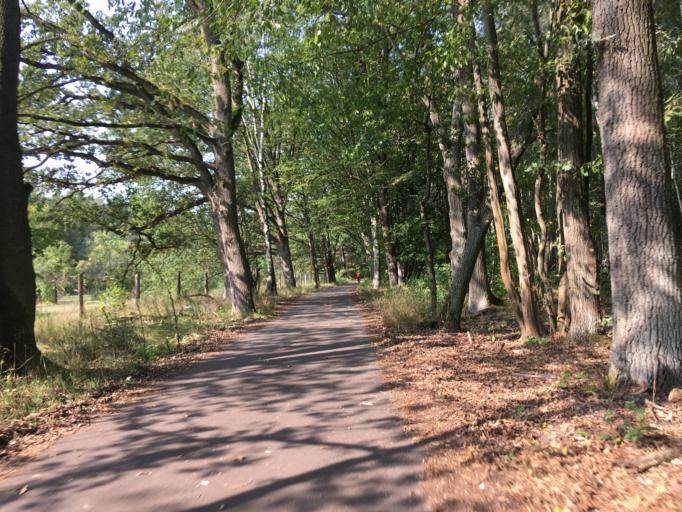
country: DE
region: Berlin
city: Hakenfelde
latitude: 52.5920
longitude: 13.1873
